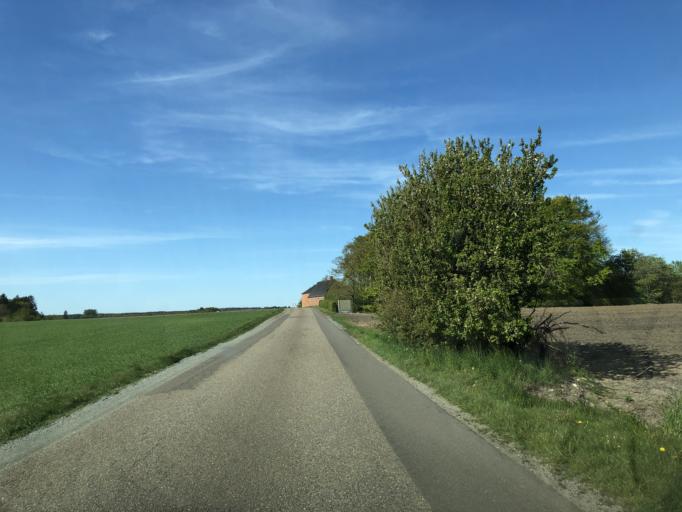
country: DK
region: Central Jutland
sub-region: Ringkobing-Skjern Kommune
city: Videbaek
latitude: 56.1762
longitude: 8.5228
